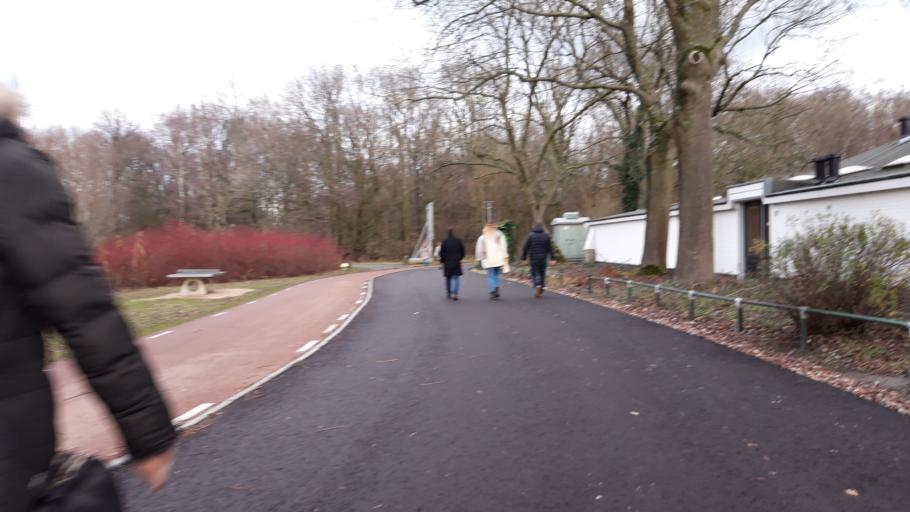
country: NL
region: South Holland
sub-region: Gemeente Rotterdam
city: Rotterdam
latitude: 51.9399
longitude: 4.5075
